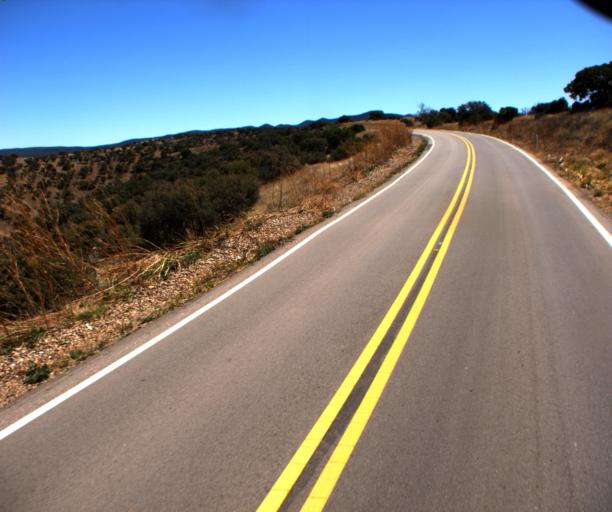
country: US
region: Arizona
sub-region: Cochise County
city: Huachuca City
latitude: 31.5278
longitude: -110.5028
